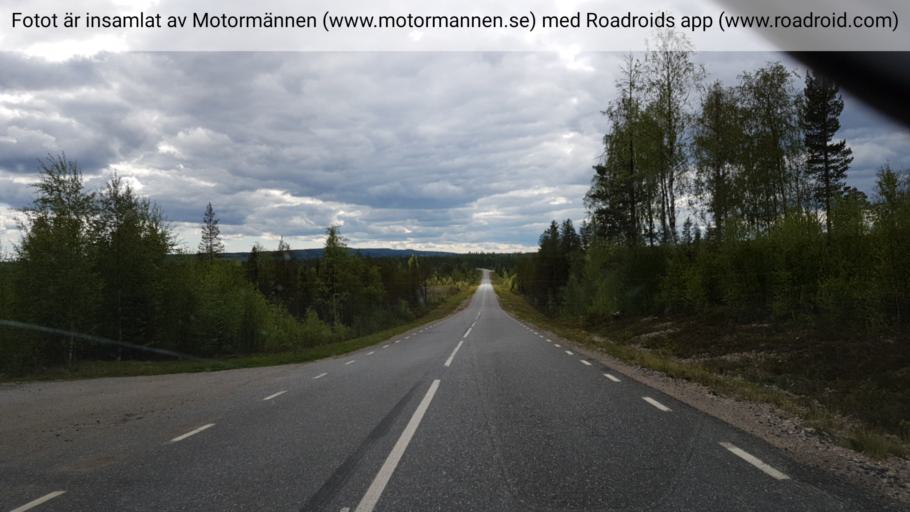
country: SE
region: Vaesterbotten
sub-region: Vindelns Kommun
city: Vindeln
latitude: 64.5203
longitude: 19.7996
